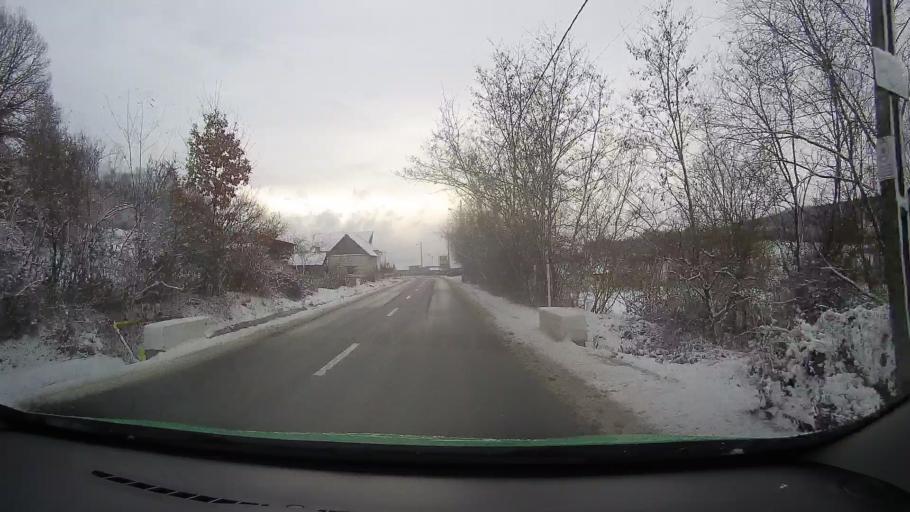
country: RO
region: Hunedoara
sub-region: Oras Hateg
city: Hateg
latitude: 45.6319
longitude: 22.9294
